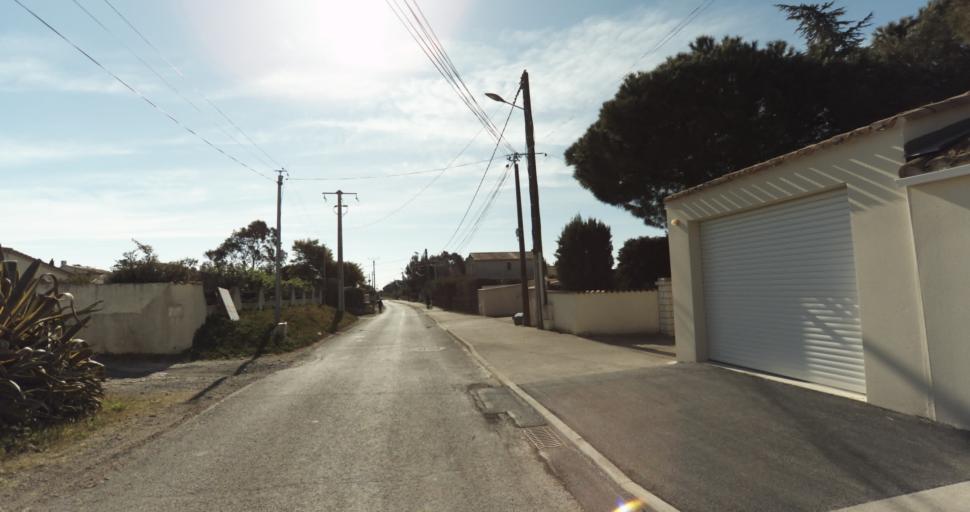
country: FR
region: Languedoc-Roussillon
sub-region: Departement de l'Herault
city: Marseillan
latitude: 43.3351
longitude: 3.5169
